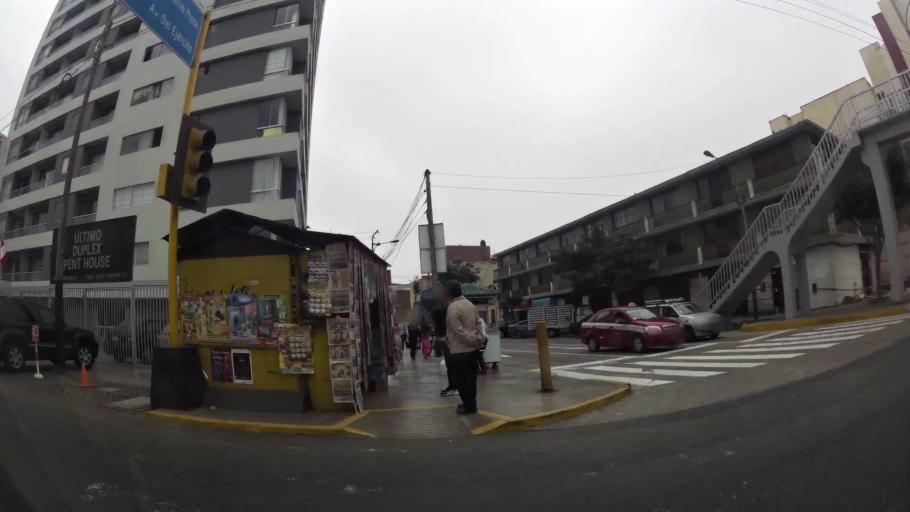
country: PE
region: Lima
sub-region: Lima
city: San Isidro
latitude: -12.0931
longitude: -77.0689
